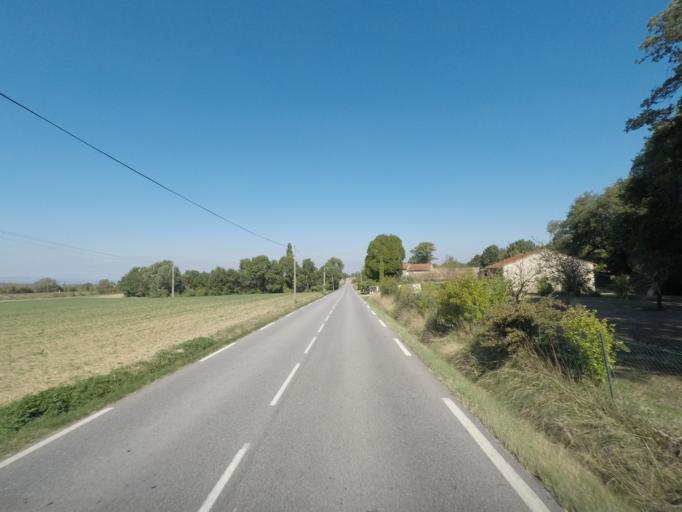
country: FR
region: Rhone-Alpes
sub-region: Departement de la Drome
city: Montmeyran
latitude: 44.8252
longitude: 5.0096
